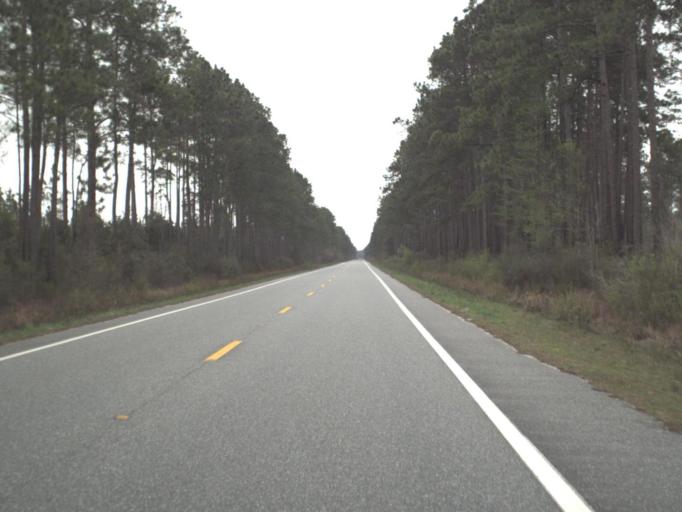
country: US
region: Florida
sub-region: Franklin County
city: Apalachicola
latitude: 29.8772
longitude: -84.9758
